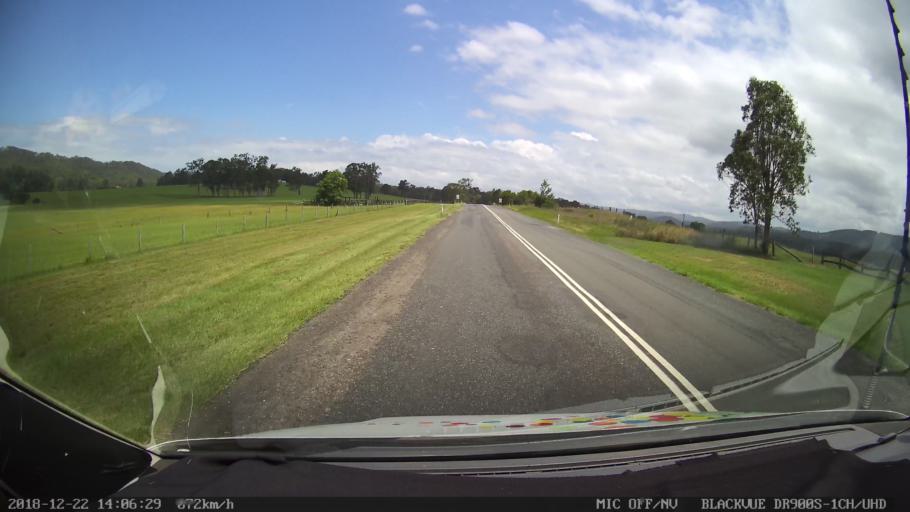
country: AU
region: New South Wales
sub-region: Clarence Valley
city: Coutts Crossing
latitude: -29.9560
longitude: 152.7275
